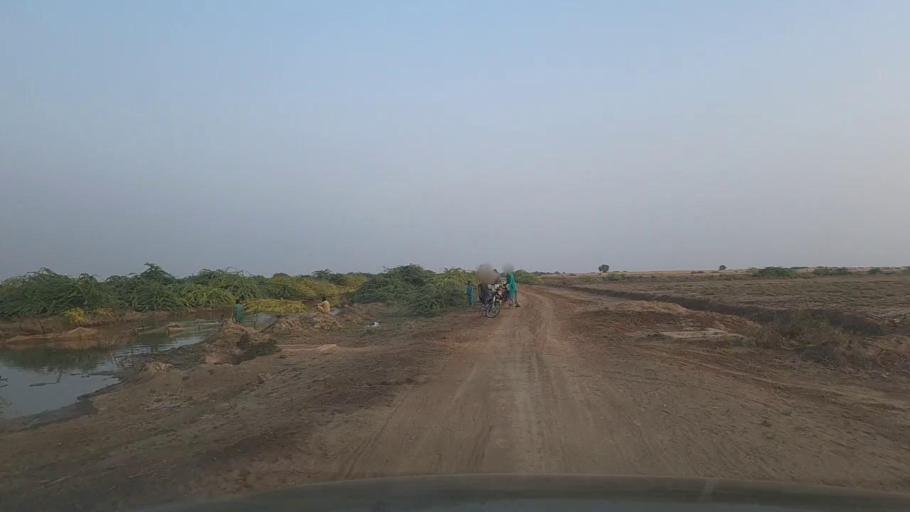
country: PK
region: Sindh
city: Jati
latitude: 24.5374
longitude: 68.4062
